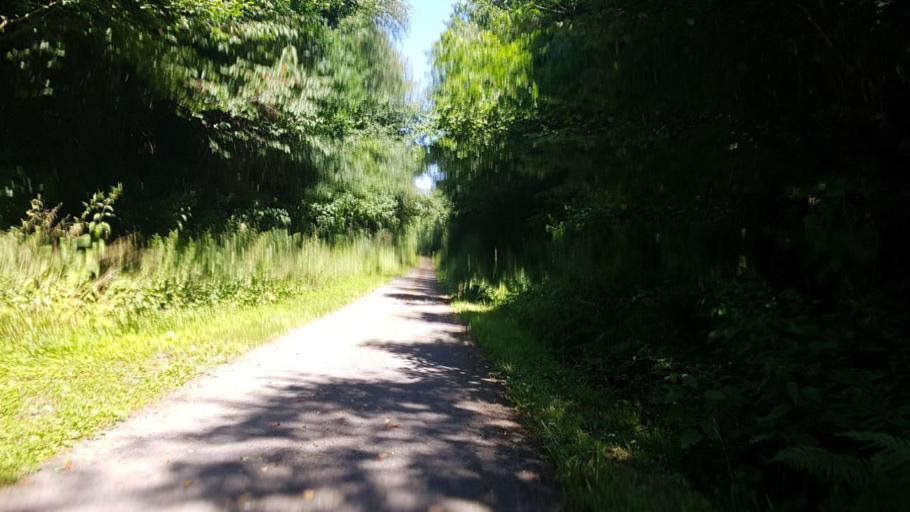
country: BE
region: Wallonia
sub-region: Province du Hainaut
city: Beaumont
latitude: 50.1990
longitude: 4.2286
